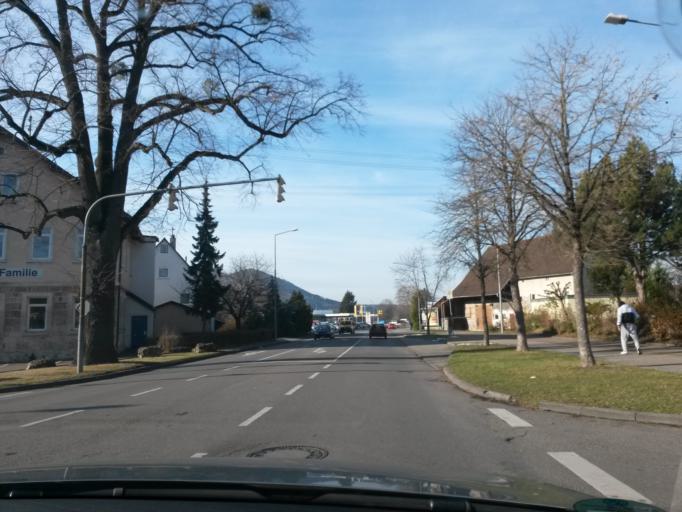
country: DE
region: Baden-Wuerttemberg
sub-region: Regierungsbezirk Stuttgart
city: Geislingen an der Steige
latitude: 48.6284
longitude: 9.8203
